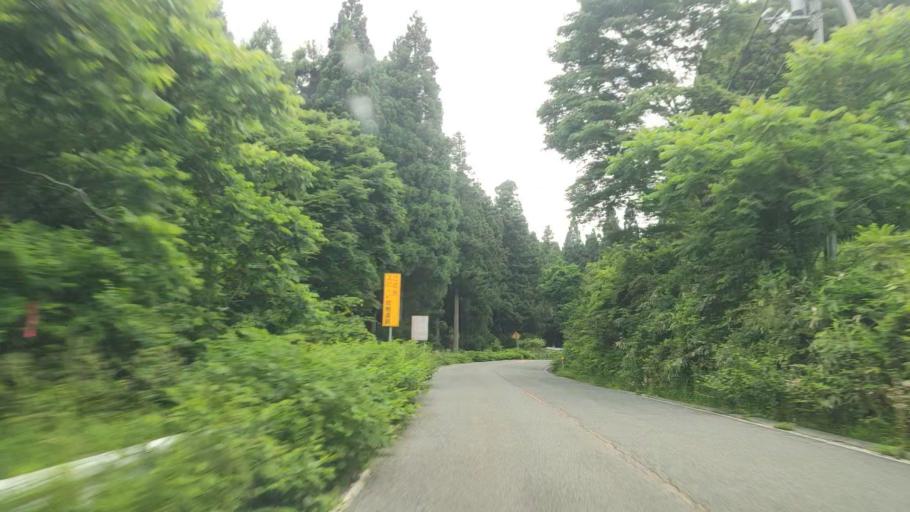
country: JP
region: Tottori
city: Yonago
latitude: 35.3283
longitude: 133.5572
